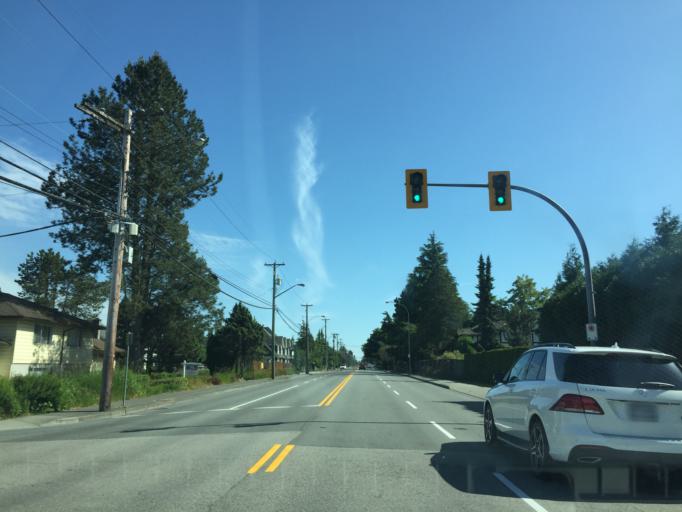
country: CA
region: British Columbia
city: Richmond
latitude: 49.1519
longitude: -123.1367
